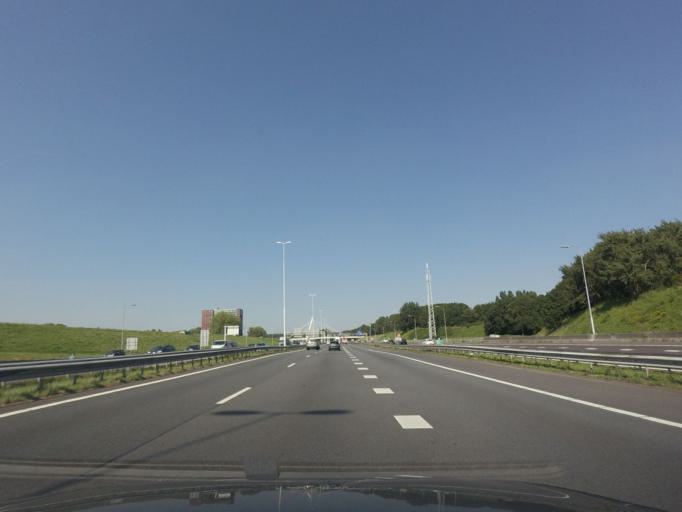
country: NL
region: South Holland
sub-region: Gemeente Capelle aan den IJssel
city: Capelle-West
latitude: 51.8857
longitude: 4.5639
